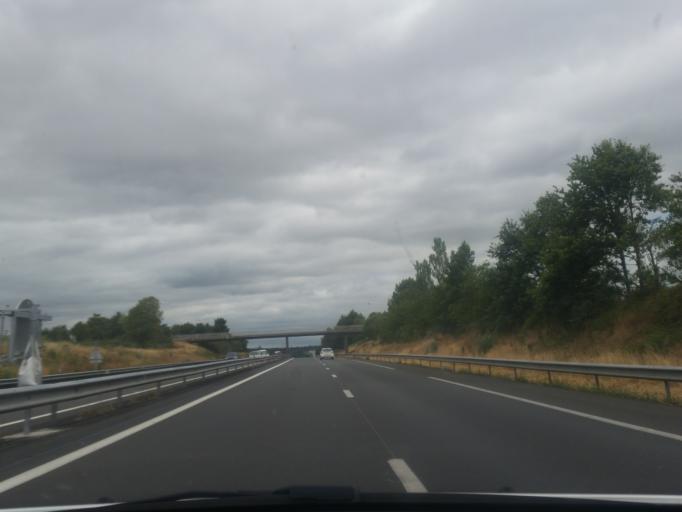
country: FR
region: Pays de la Loire
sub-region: Departement de Maine-et-Loire
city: Durtal
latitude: 47.6358
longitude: -0.2748
